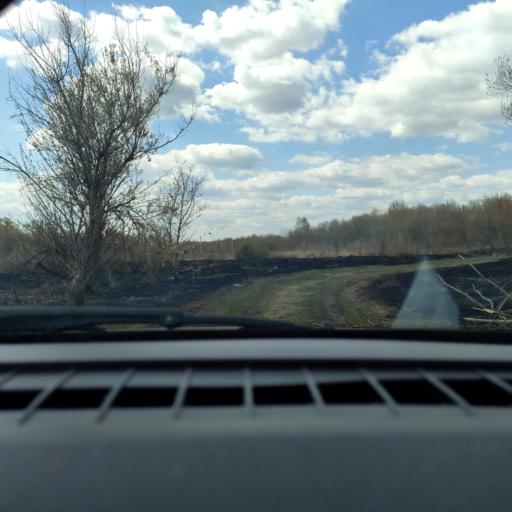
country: RU
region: Samara
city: Krotovka
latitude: 53.5346
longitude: 51.1485
